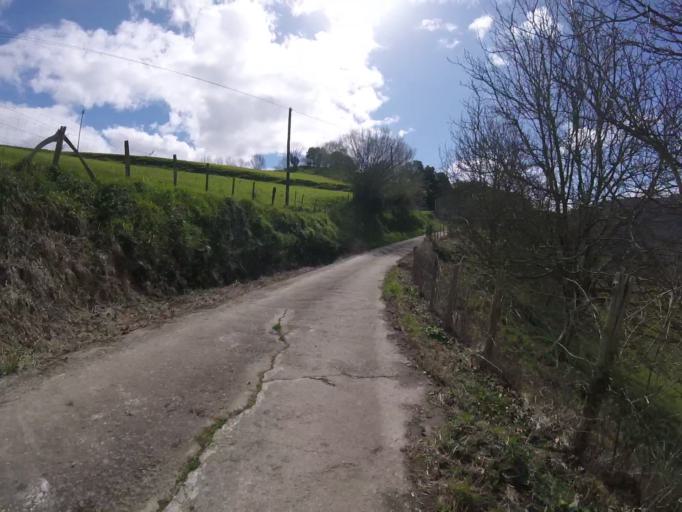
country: ES
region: Basque Country
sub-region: Provincia de Guipuzcoa
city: Albiztur
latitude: 43.1360
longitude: -2.1271
